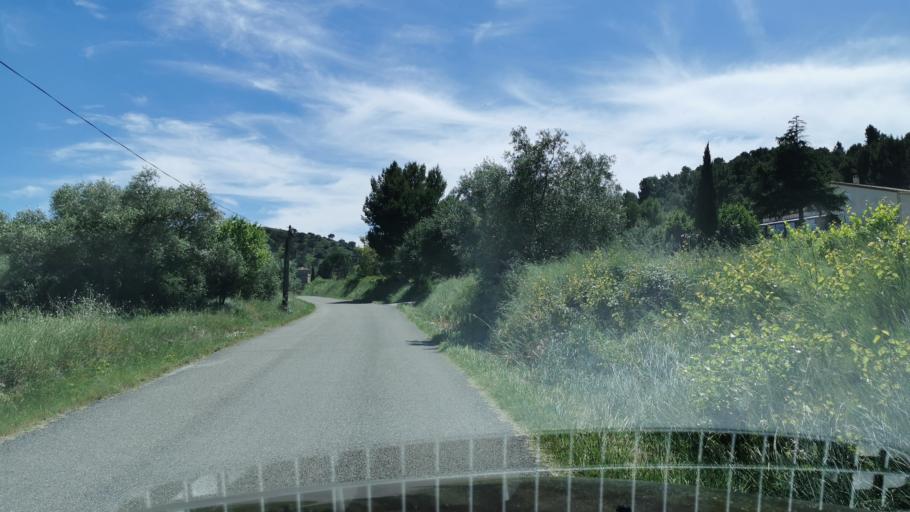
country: FR
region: Languedoc-Roussillon
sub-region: Departement de l'Aude
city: Nevian
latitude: 43.2053
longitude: 2.9033
